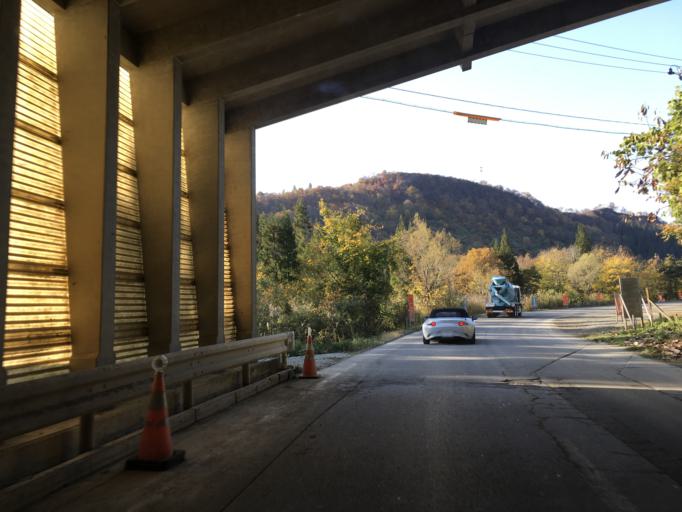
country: JP
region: Akita
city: Yuzawa
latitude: 39.0642
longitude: 140.7204
